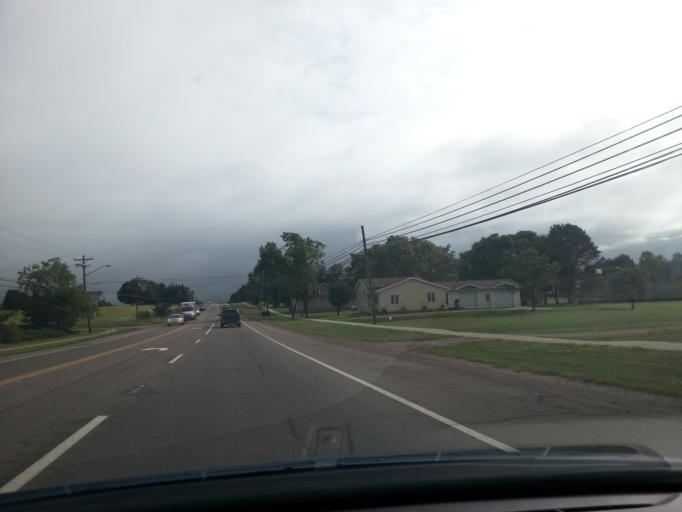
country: CA
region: Prince Edward Island
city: Charlottetown
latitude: 46.2799
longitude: -63.0998
